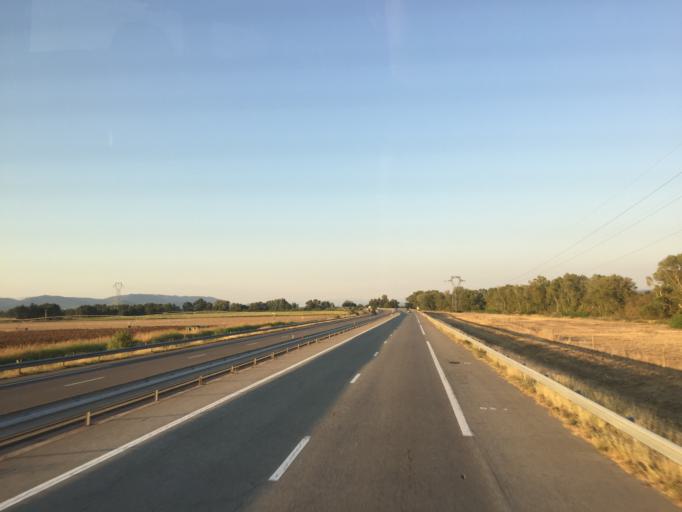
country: FR
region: Provence-Alpes-Cote d'Azur
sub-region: Departement des Alpes-de-Haute-Provence
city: Sainte-Tulle
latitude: 43.7571
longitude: 5.7741
